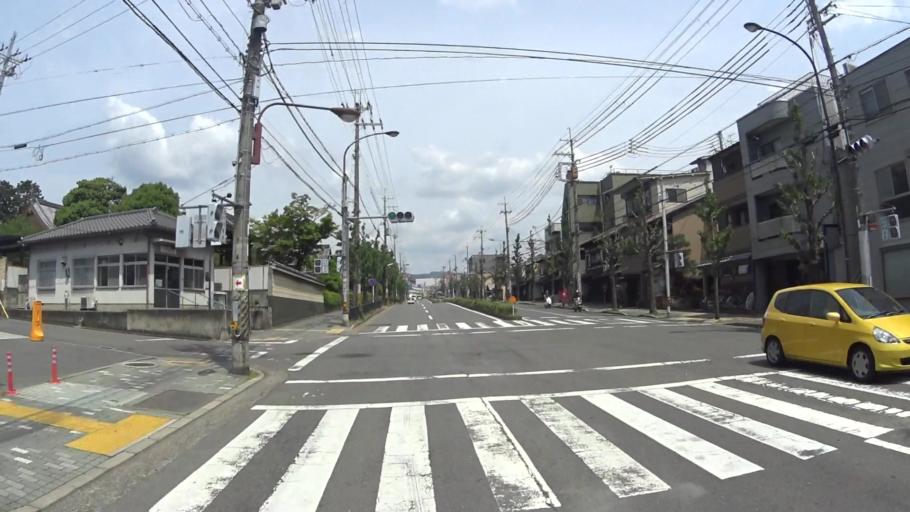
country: JP
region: Kyoto
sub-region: Kyoto-shi
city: Kamigyo-ku
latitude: 35.0375
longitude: 135.7397
